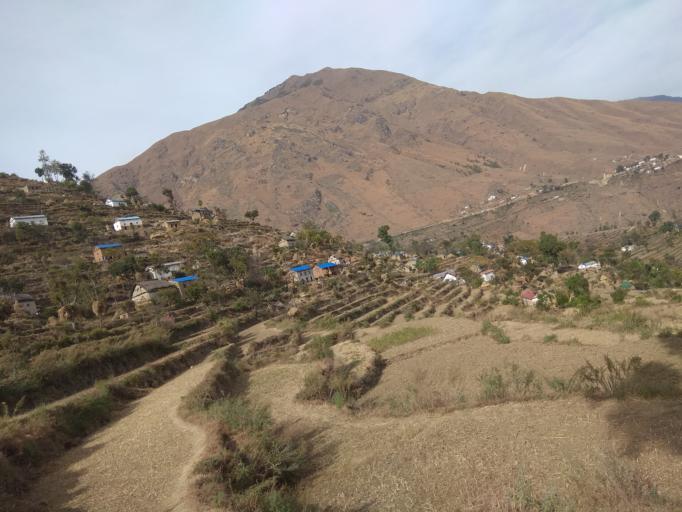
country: NP
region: Mid Western
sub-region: Bheri Zone
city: Dailekh
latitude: 29.2489
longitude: 81.6714
